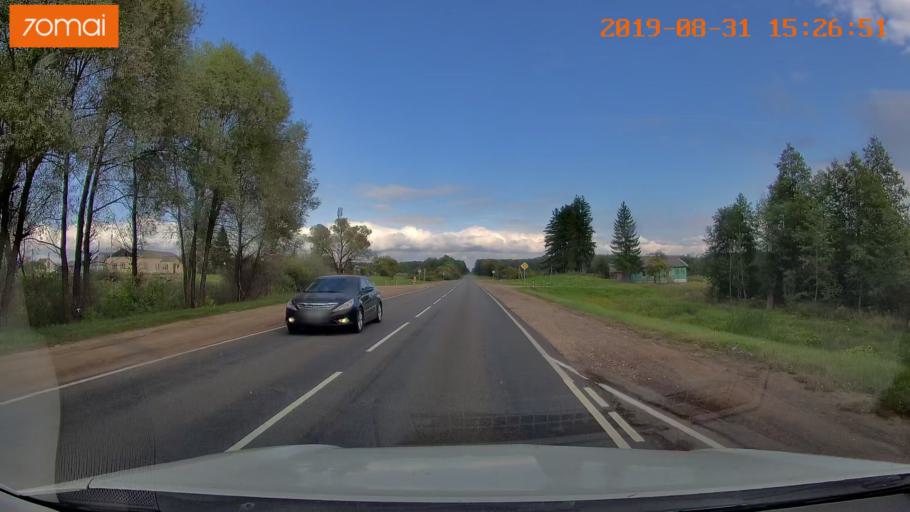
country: RU
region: Kaluga
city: Baryatino
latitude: 54.5525
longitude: 34.5467
